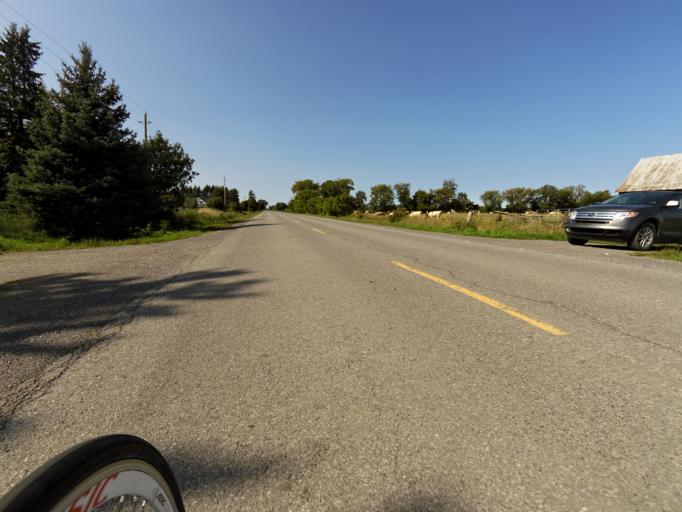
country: CA
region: Ontario
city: Carleton Place
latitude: 45.3396
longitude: -76.0995
